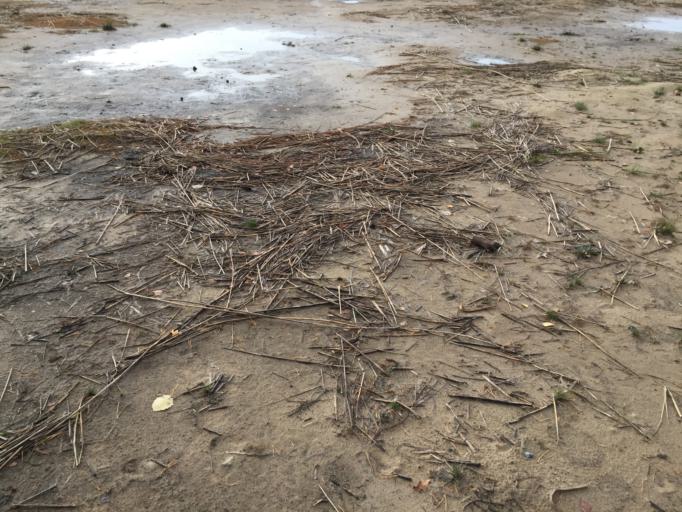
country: SE
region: OErebro
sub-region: Orebro Kommun
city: Odensbacken
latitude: 59.0527
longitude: 15.5519
